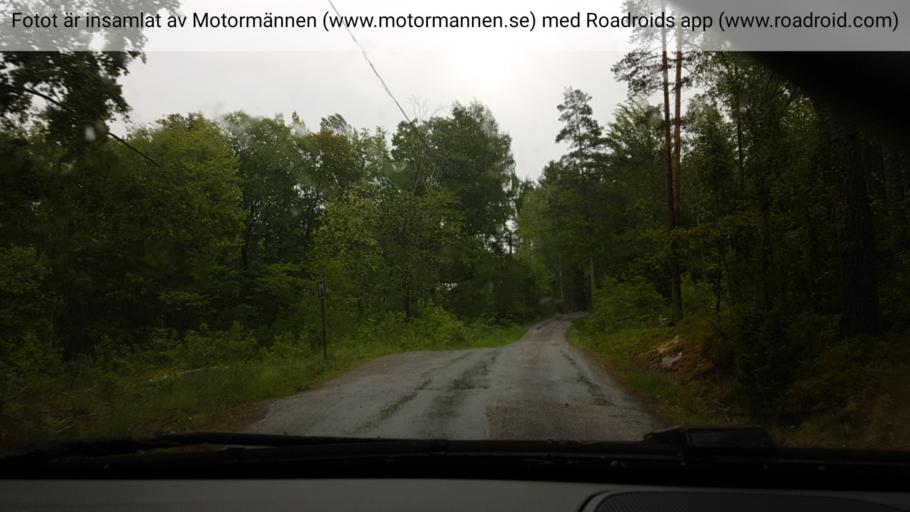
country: SE
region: Stockholm
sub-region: Haninge Kommun
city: Jordbro
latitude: 59.0181
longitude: 18.1132
